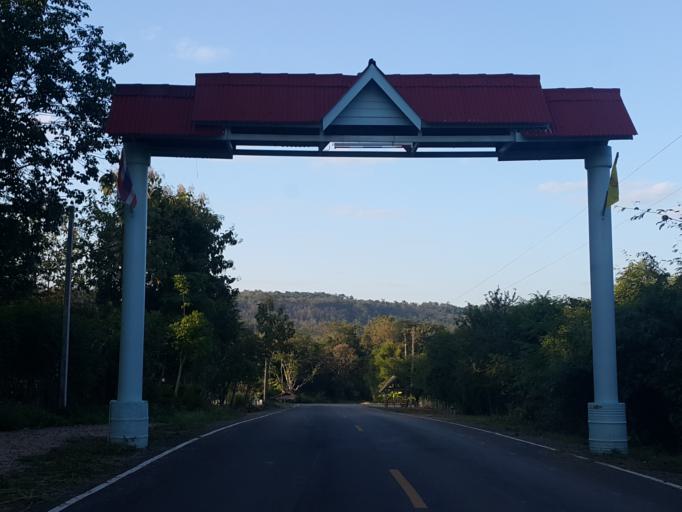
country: TH
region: Lampang
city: Lampang
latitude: 18.4368
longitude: 99.5701
